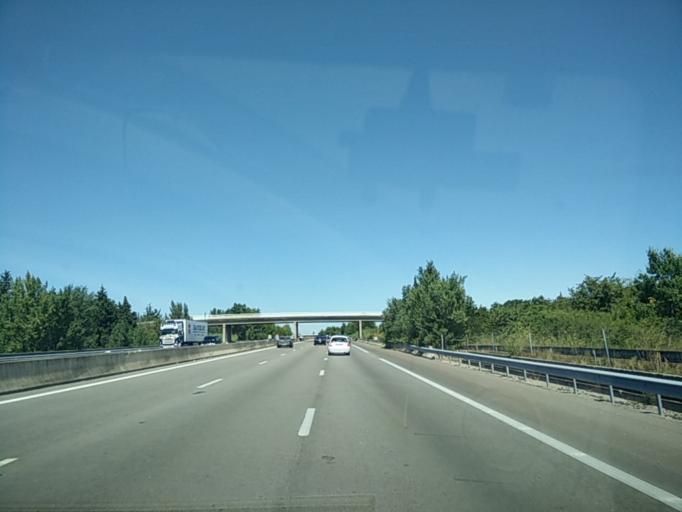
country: FR
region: Provence-Alpes-Cote d'Azur
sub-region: Departement du Vaucluse
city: Morieres-les-Avignon
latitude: 43.9416
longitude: 4.9116
